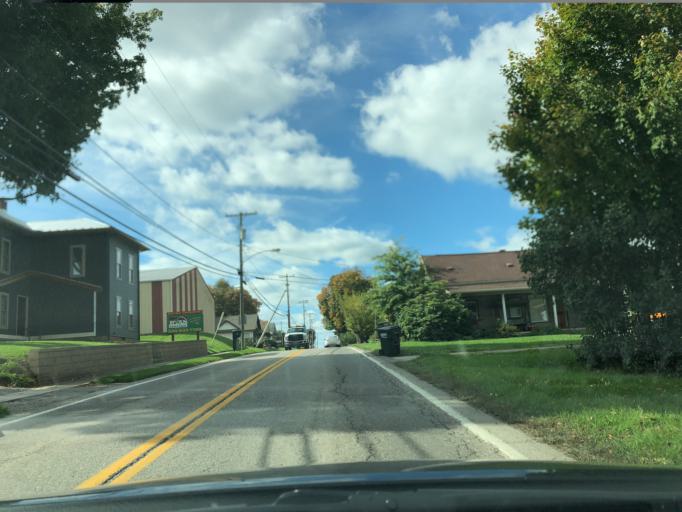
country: US
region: Ohio
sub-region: Stark County
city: Beach City
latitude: 40.6563
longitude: -81.6349
